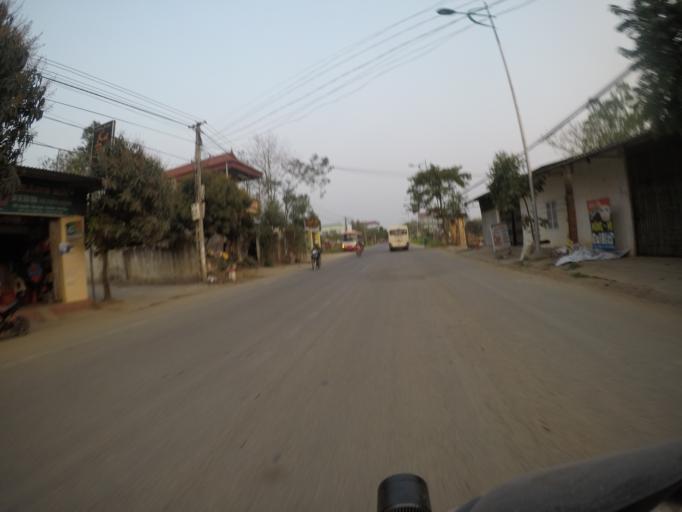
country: VN
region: Vinh Phuc
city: Trai Ngau
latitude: 21.4255
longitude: 105.5936
